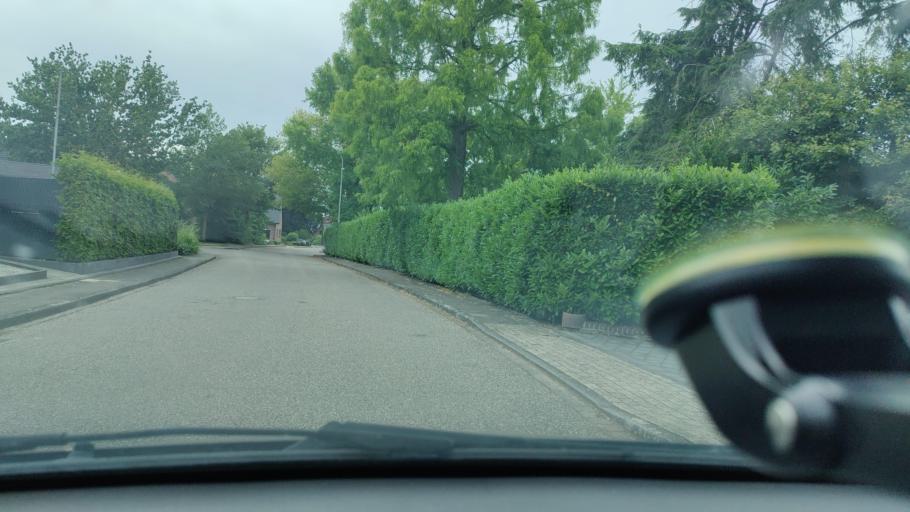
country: DE
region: North Rhine-Westphalia
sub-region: Regierungsbezirk Dusseldorf
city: Sonsbeck
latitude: 51.5747
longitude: 6.3672
